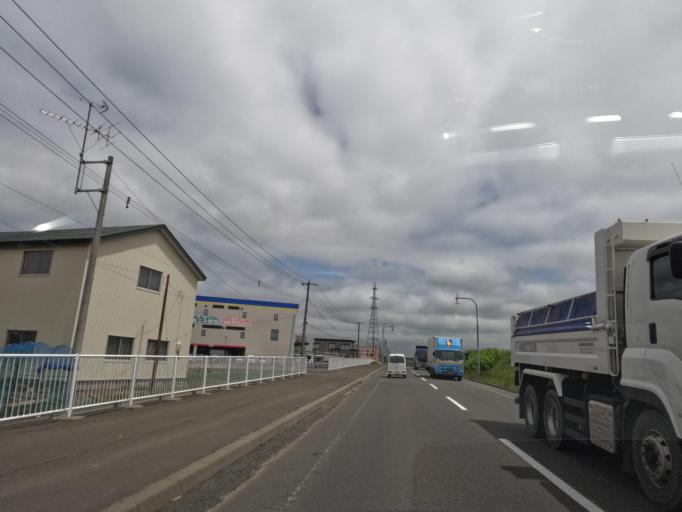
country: JP
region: Hokkaido
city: Sapporo
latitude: 43.0790
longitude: 141.4069
